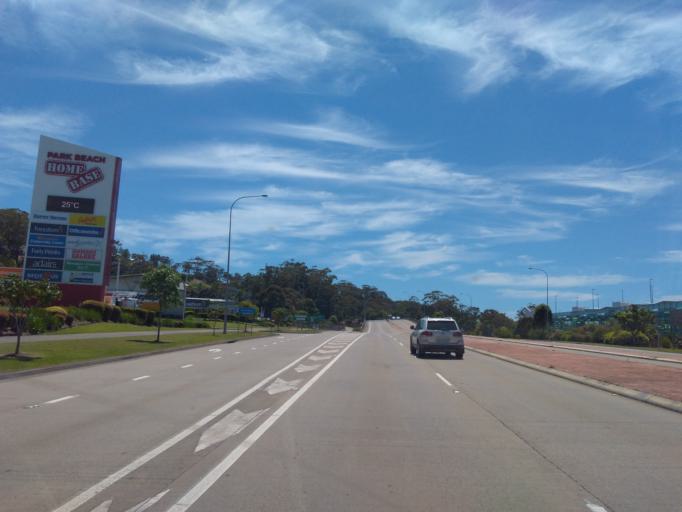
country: AU
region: New South Wales
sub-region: Coffs Harbour
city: Coffs Harbour
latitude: -30.2820
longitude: 153.1287
